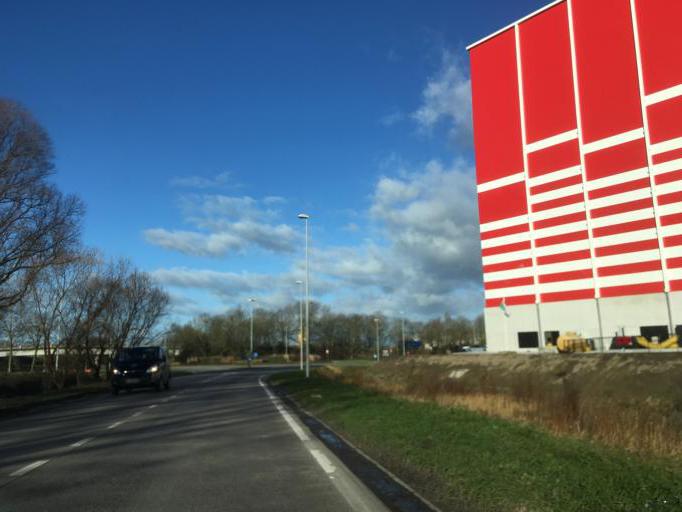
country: BE
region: Flanders
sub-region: Provincie West-Vlaanderen
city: Roeselare
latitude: 50.9404
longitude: 3.1651
